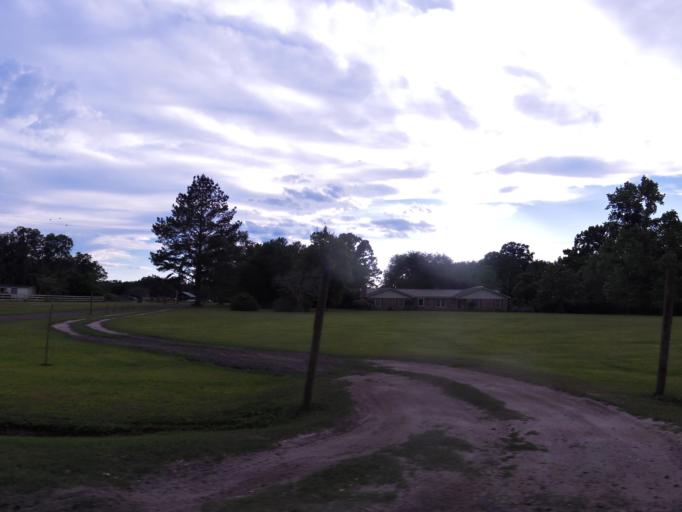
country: US
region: South Carolina
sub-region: Jasper County
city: Hardeeville
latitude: 32.3199
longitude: -81.0891
